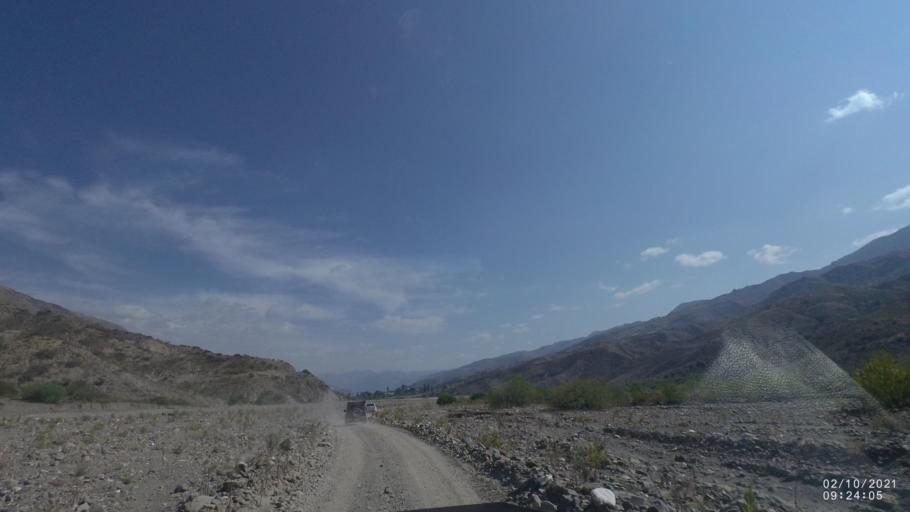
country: BO
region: Cochabamba
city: Irpa Irpa
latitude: -17.8652
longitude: -66.3122
